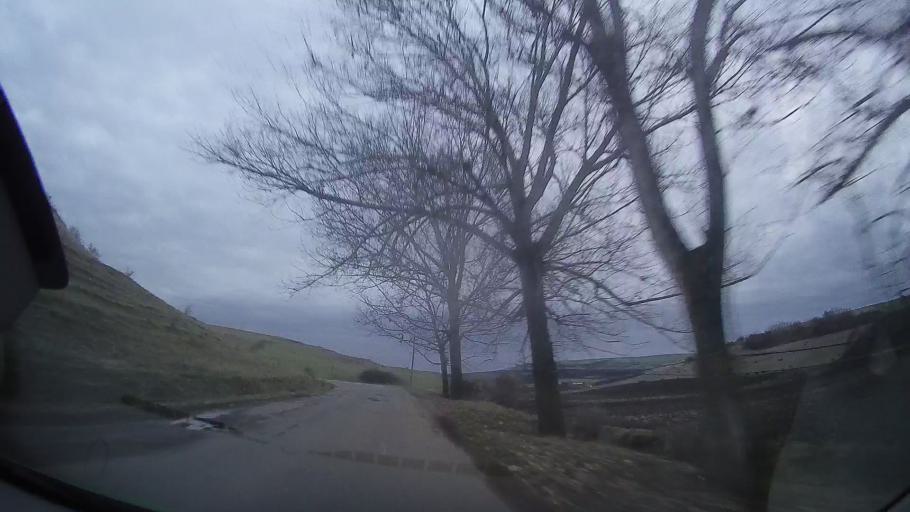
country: RO
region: Cluj
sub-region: Comuna Caianu
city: Vaida-Camaras
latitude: 46.8188
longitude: 23.9357
